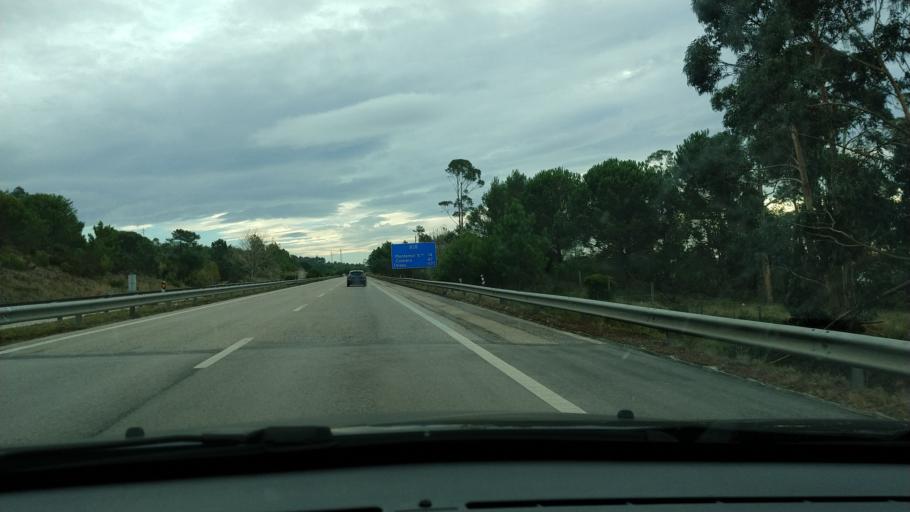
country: PT
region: Coimbra
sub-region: Figueira da Foz
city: Tavarede
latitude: 40.1496
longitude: -8.8259
